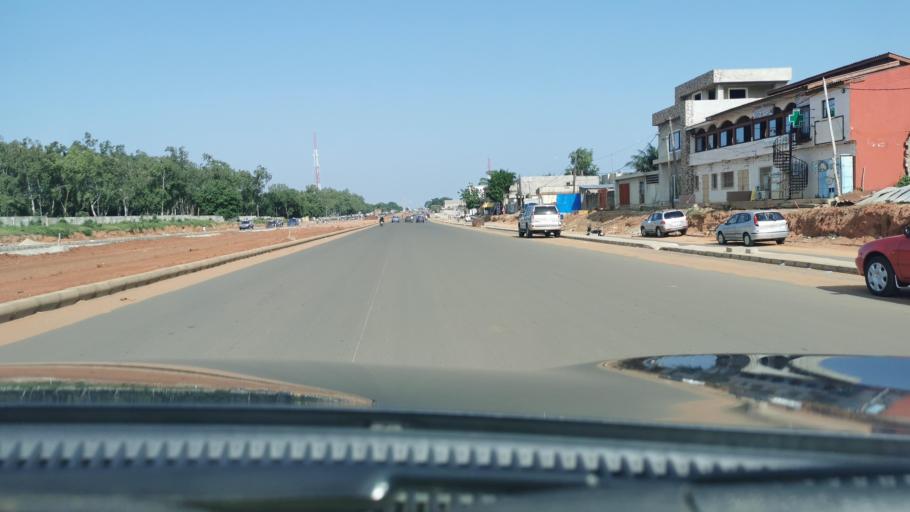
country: TG
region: Maritime
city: Lome
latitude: 6.1924
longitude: 1.1582
